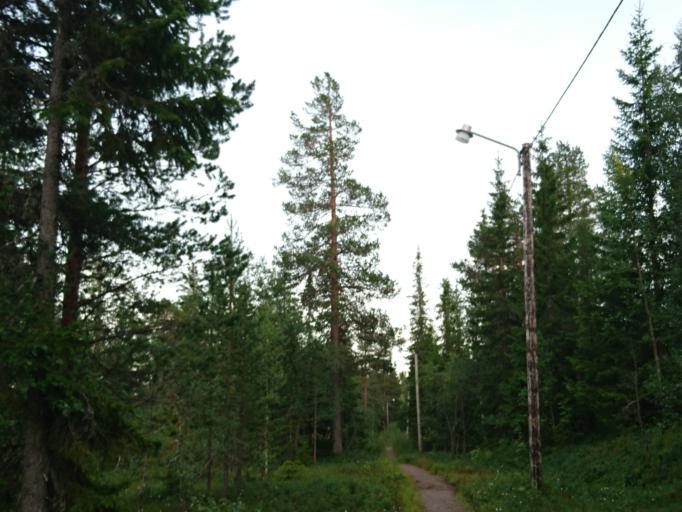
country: SE
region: Dalarna
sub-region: Malung-Saelens kommun
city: Malung
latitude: 61.1715
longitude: 13.1701
